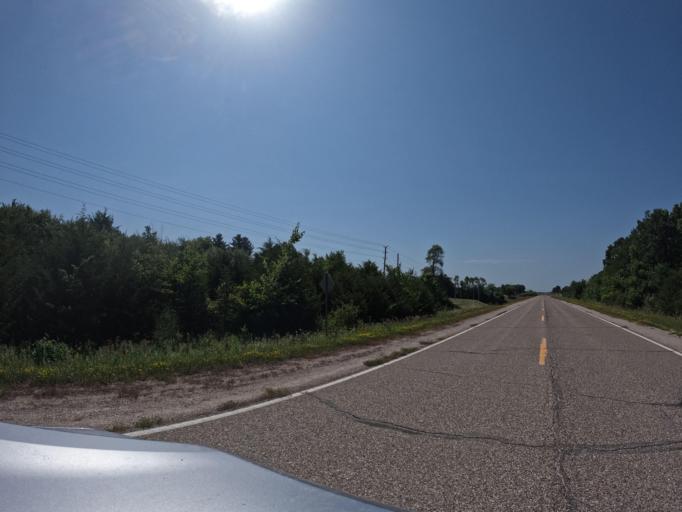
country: US
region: Iowa
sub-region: Henry County
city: Mount Pleasant
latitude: 40.9359
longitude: -91.5401
